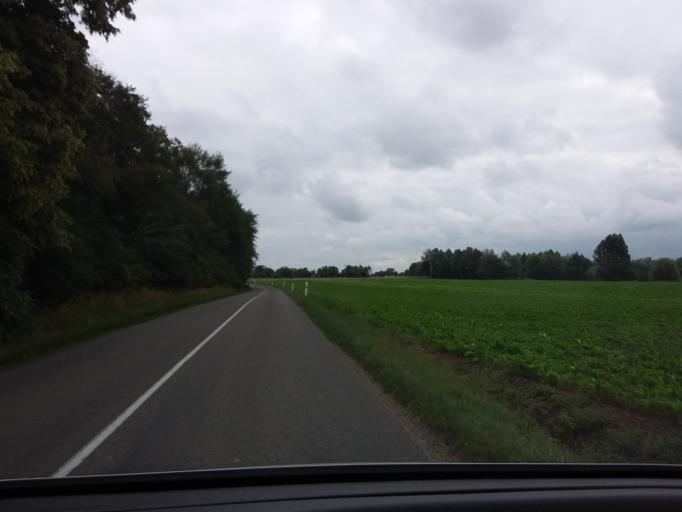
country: FR
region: Champagne-Ardenne
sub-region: Departement de la Marne
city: Cormicy
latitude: 49.4031
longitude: 3.8054
